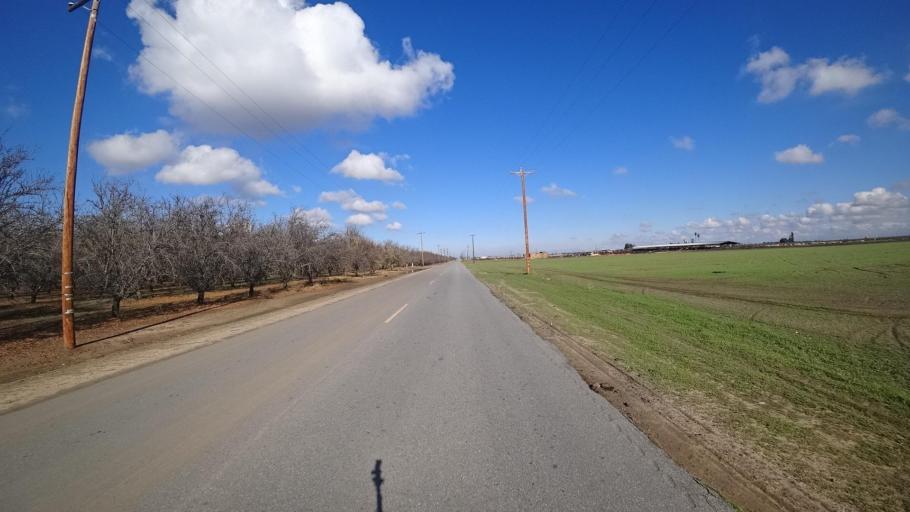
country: US
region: California
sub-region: Kern County
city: McFarland
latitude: 35.6552
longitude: -119.2409
